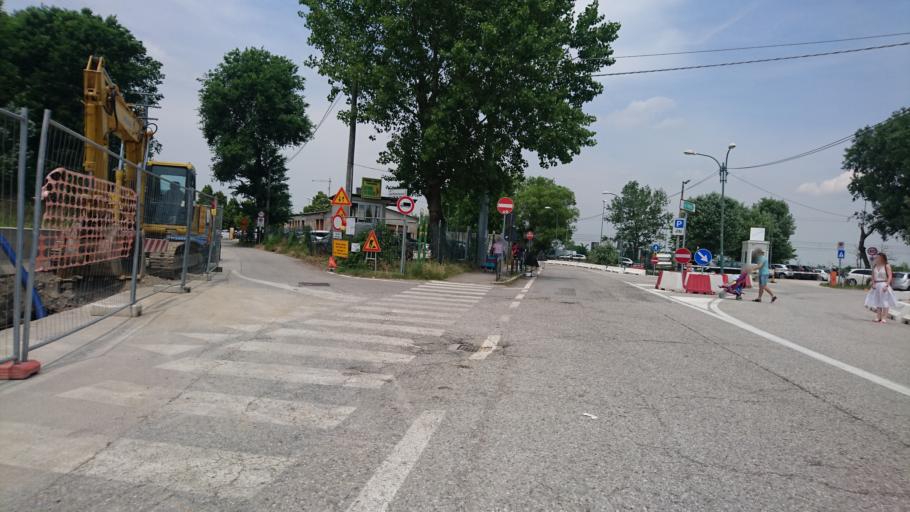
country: IT
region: Veneto
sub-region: Provincia di Venezia
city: Campalto
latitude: 45.4686
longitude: 12.2657
